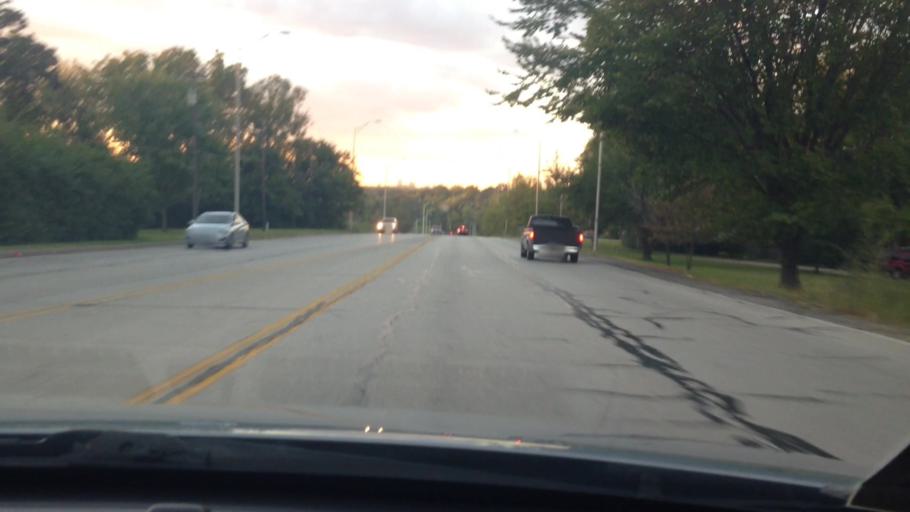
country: US
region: Missouri
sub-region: Jackson County
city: Raytown
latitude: 39.0258
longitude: -94.5053
